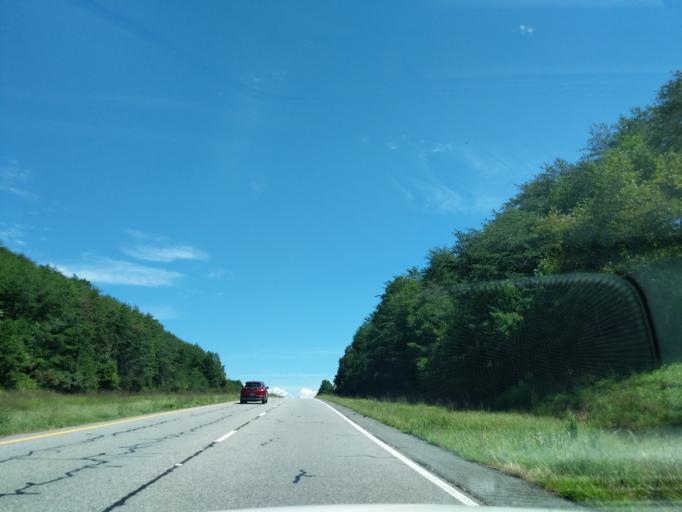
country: US
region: Georgia
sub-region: Fannin County
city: Blue Ridge
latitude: 34.8905
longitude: -84.2342
